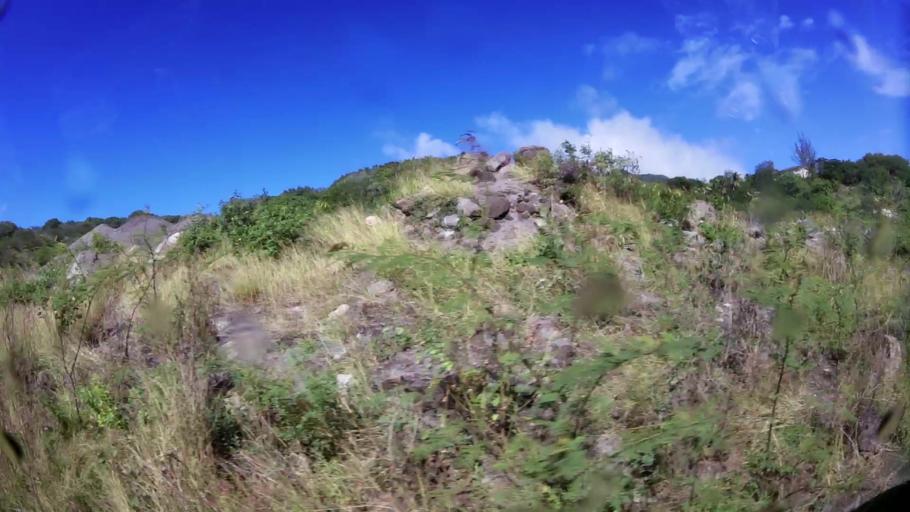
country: MS
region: Saint Peter
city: Saint Peters
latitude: 16.7417
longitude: -62.2224
